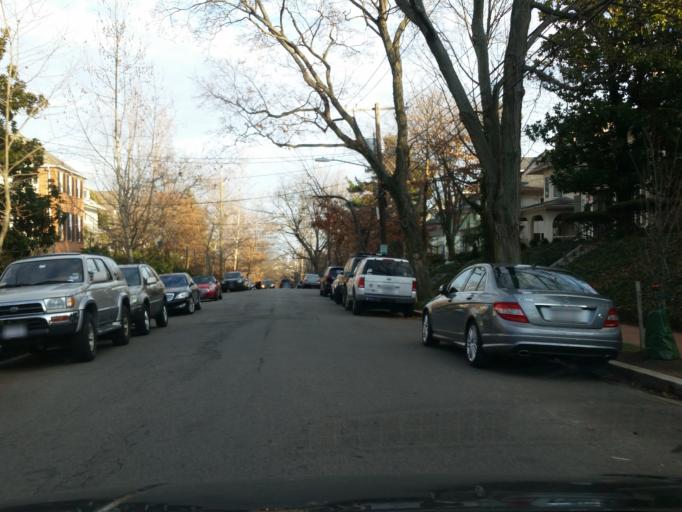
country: US
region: Maryland
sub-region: Montgomery County
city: Friendship Village
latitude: 38.9335
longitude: -77.0703
